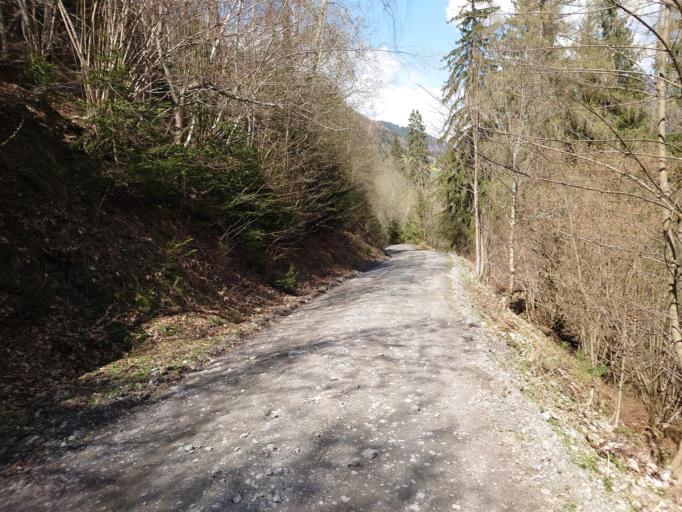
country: AT
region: Salzburg
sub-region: Politischer Bezirk Zell am See
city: Bruck an der Grossglocknerstrasse
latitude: 47.2399
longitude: 12.8192
